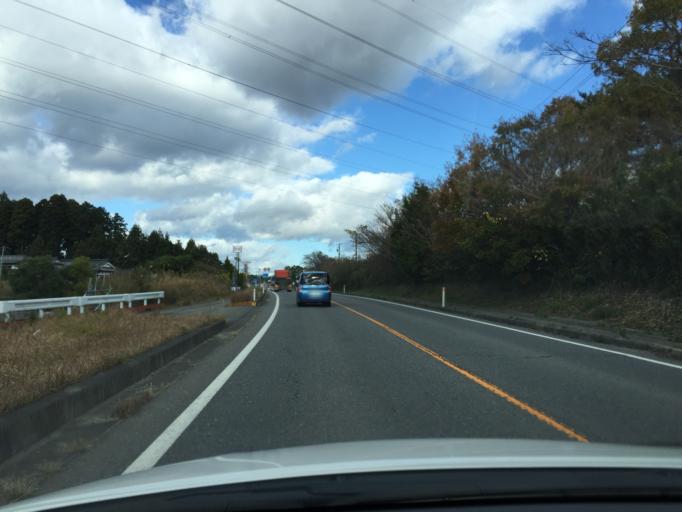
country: JP
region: Fukushima
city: Namie
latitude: 37.3998
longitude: 141.0016
